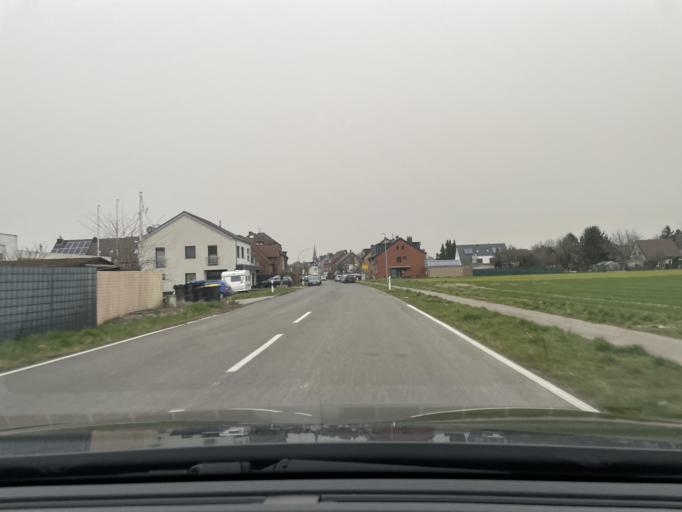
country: DE
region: North Rhine-Westphalia
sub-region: Regierungsbezirk Dusseldorf
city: Juchen
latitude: 51.0940
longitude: 6.4583
